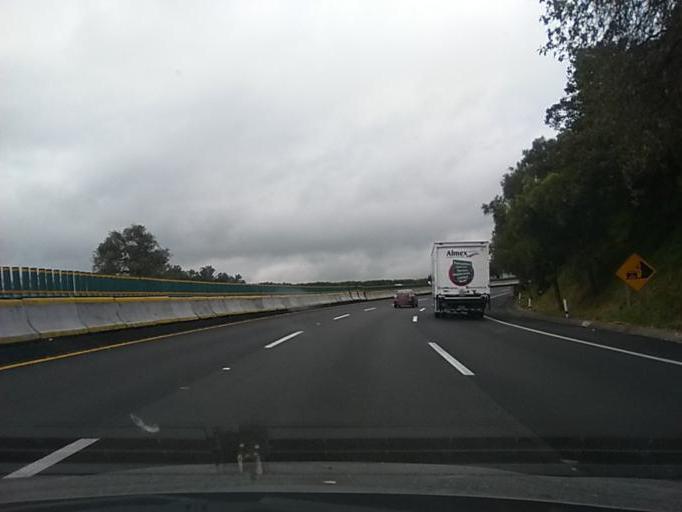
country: MX
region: Mexico City
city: Xochimilco
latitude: 19.2252
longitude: -99.1293
